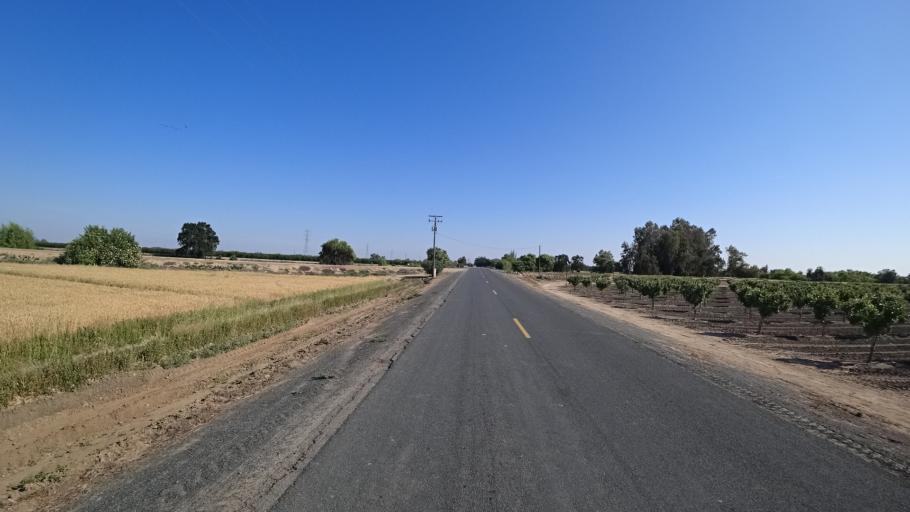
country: US
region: California
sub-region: Fresno County
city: Riverdale
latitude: 36.3730
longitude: -119.8872
